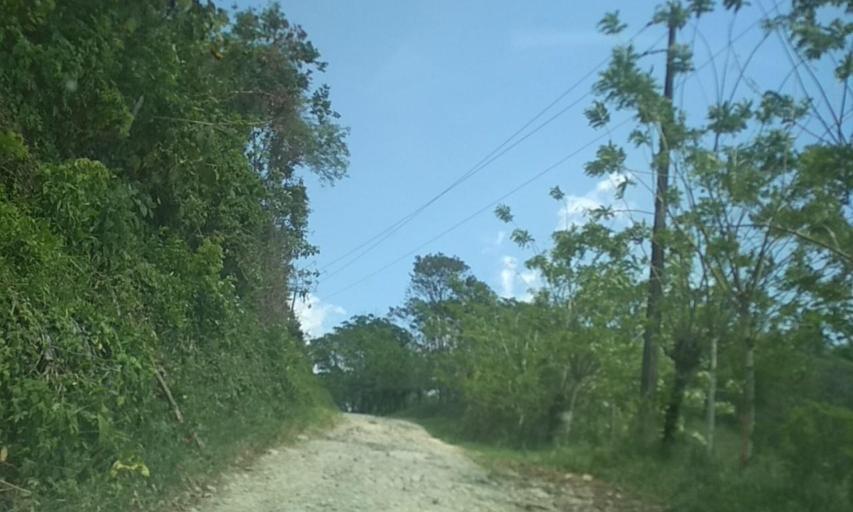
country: MX
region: Chiapas
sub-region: Tecpatan
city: Raudales Malpaso
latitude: 17.3013
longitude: -93.8222
